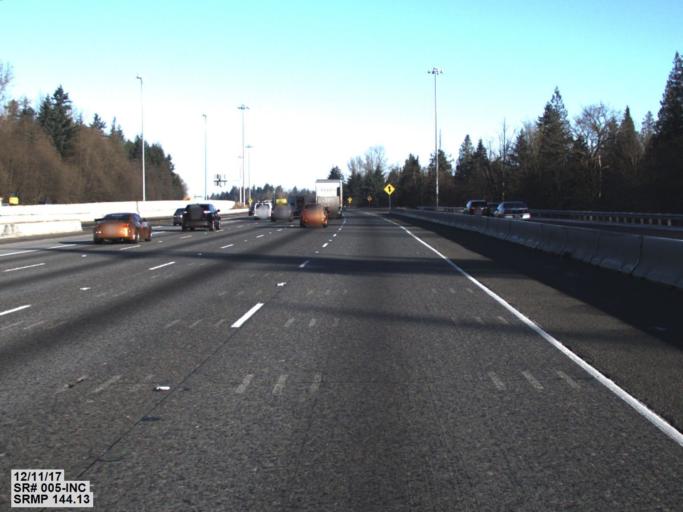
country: US
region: Washington
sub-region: King County
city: Federal Way
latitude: 47.3193
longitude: -122.2955
